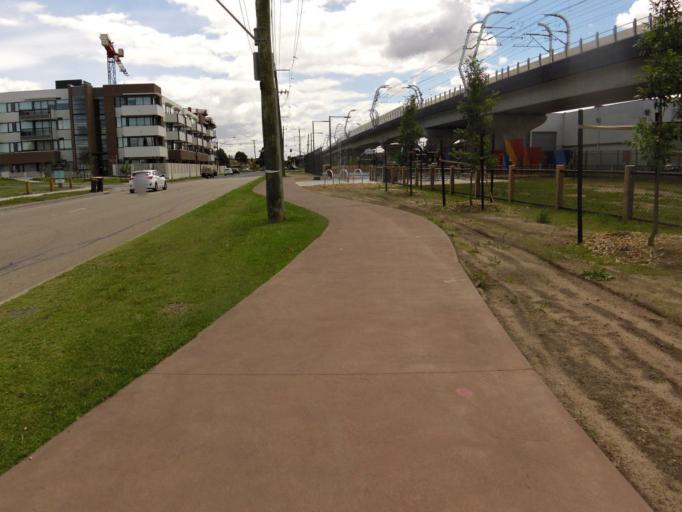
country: AU
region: Victoria
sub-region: Kingston
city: Clayton South
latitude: -37.9305
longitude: 145.1280
